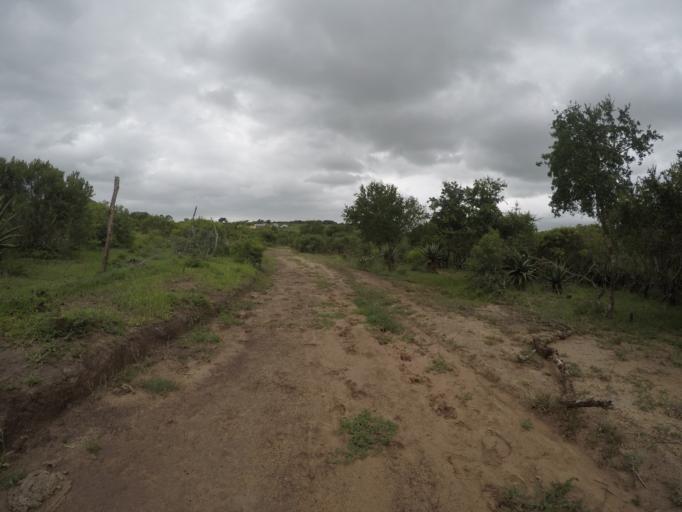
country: ZA
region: KwaZulu-Natal
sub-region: uThungulu District Municipality
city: Empangeni
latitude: -28.5956
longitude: 31.8479
